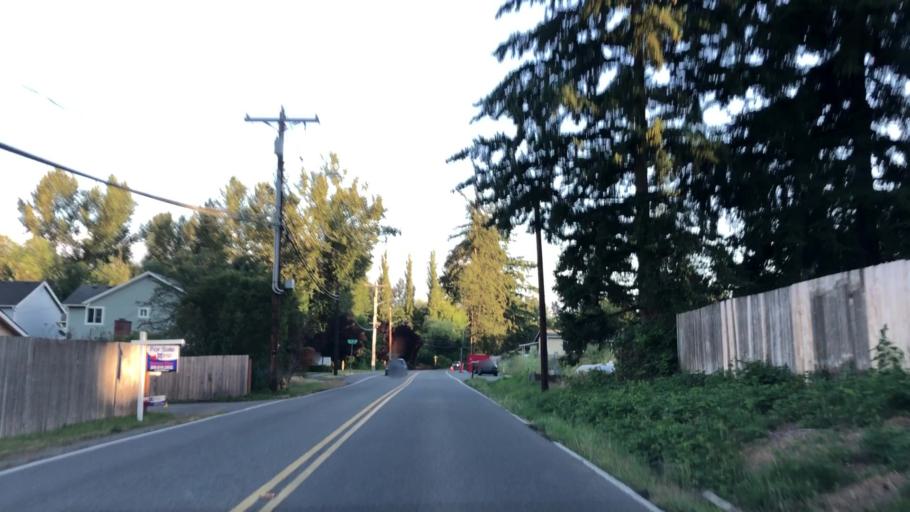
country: US
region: Washington
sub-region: Snohomish County
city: Martha Lake
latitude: 47.8640
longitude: -122.2688
